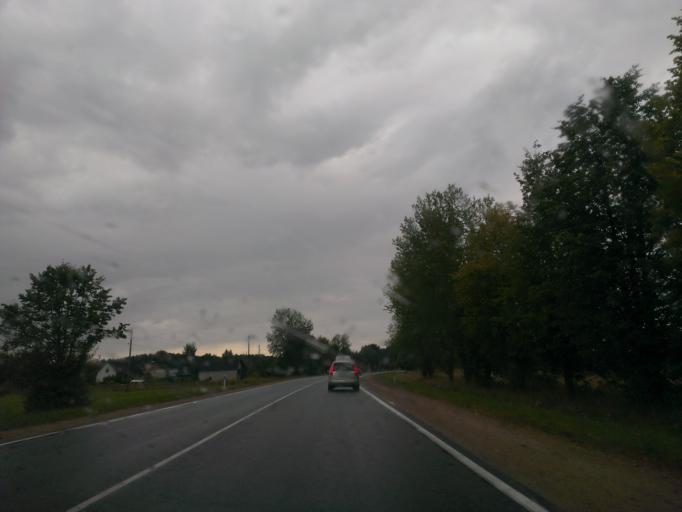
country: LV
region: Ogre
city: Ogre
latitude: 56.7754
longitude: 24.6592
